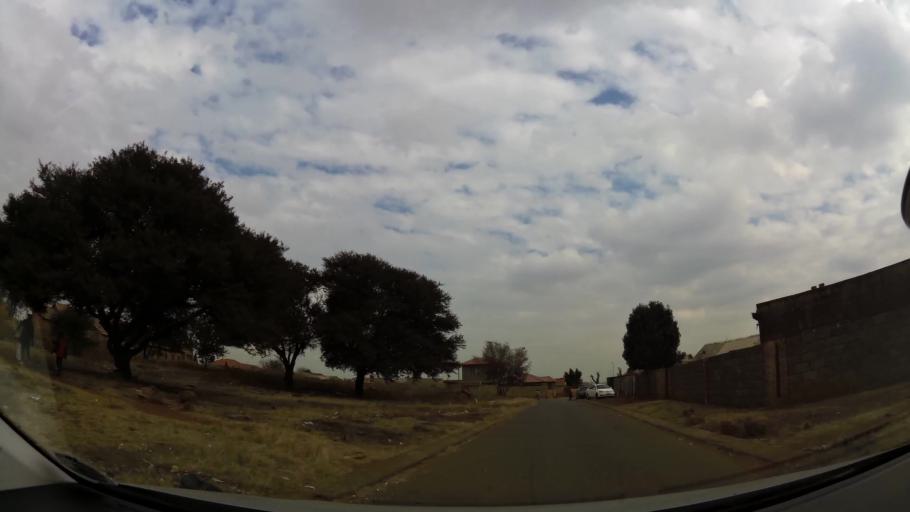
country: ZA
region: Gauteng
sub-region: City of Johannesburg Metropolitan Municipality
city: Soweto
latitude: -26.2607
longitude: 27.8518
